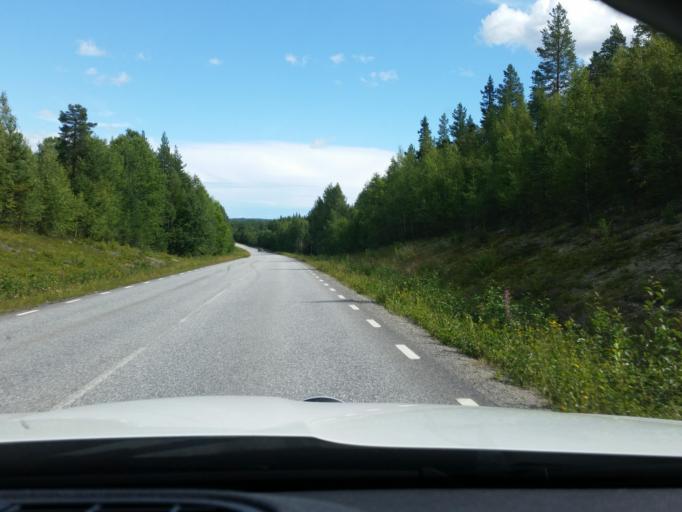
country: SE
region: Norrbotten
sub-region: Pitea Kommun
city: Hortlax
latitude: 65.2708
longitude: 21.3500
